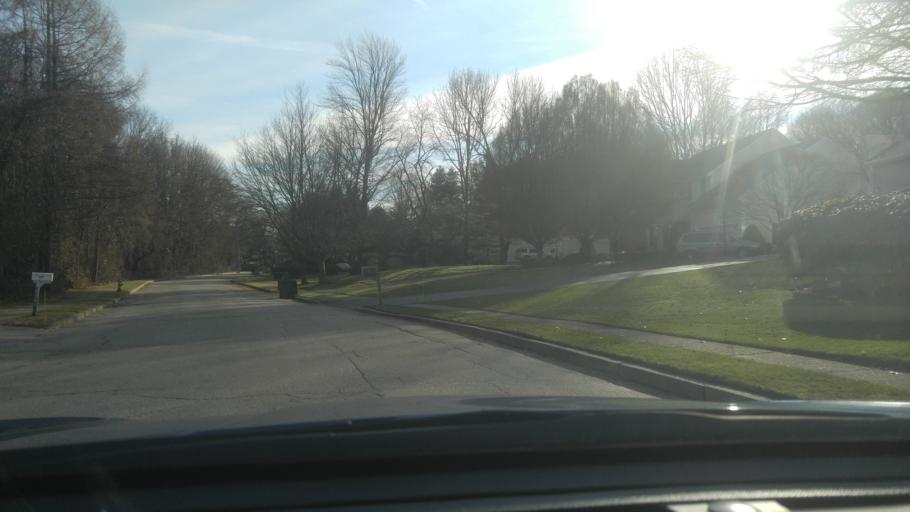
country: US
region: Rhode Island
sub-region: Kent County
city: East Greenwich
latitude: 41.6753
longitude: -71.4703
